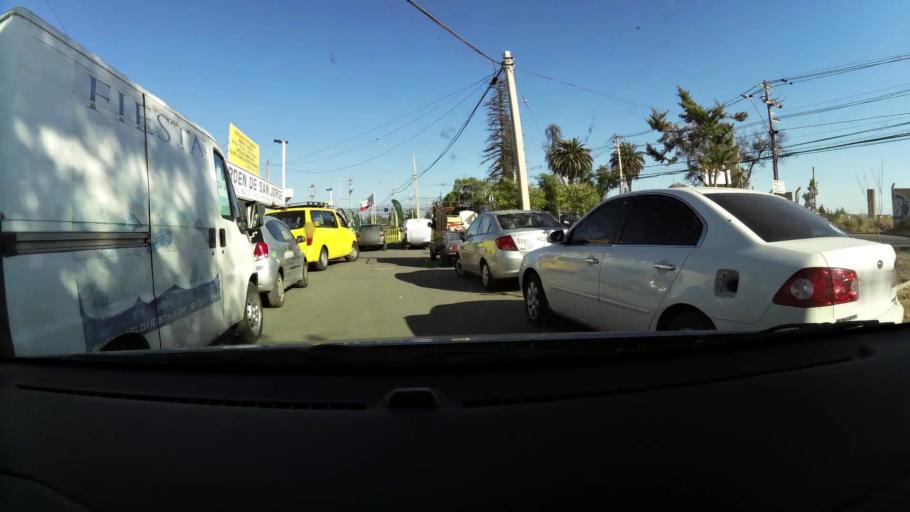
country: CL
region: Santiago Metropolitan
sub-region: Provincia de Maipo
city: San Bernardo
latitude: -33.6041
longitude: -70.6836
